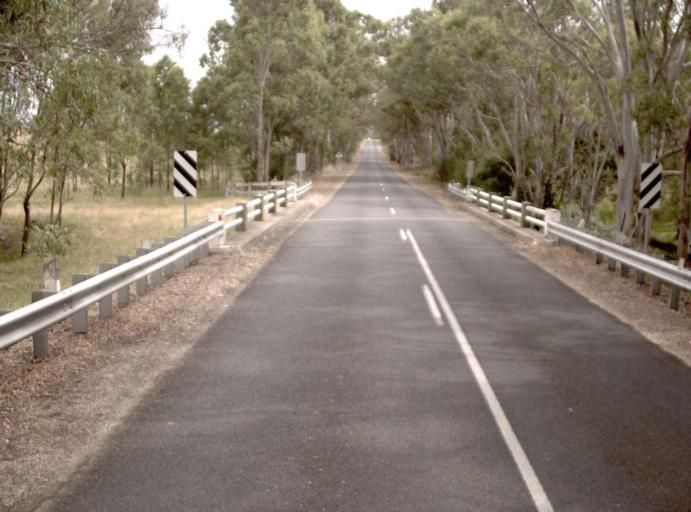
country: AU
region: Victoria
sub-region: Wellington
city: Sale
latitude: -37.8842
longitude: 147.0645
